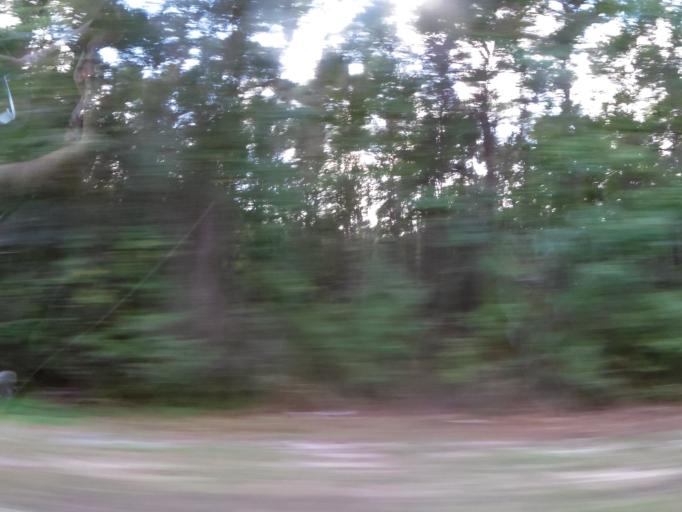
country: US
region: Georgia
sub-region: Liberty County
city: Midway
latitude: 31.6967
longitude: -81.4116
